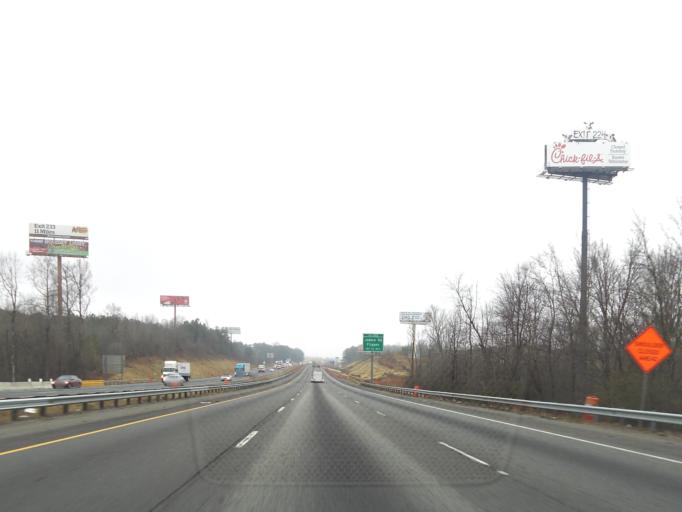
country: US
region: Georgia
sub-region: Henry County
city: McDonough
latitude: 33.4692
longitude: -84.2127
